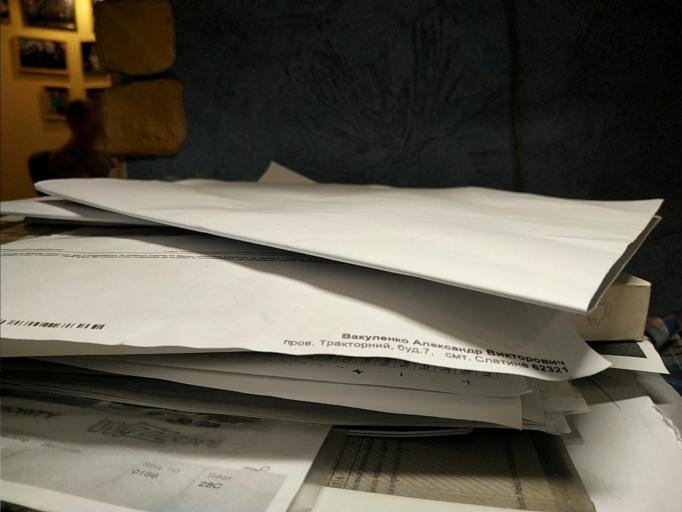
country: RU
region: Tverskaya
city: Zubtsov
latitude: 56.1322
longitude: 34.5044
